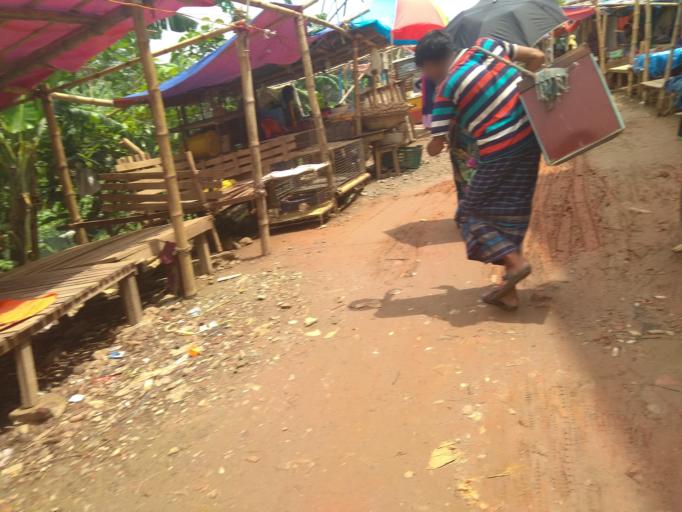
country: BD
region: Dhaka
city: Tungi
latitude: 23.8165
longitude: 90.3525
